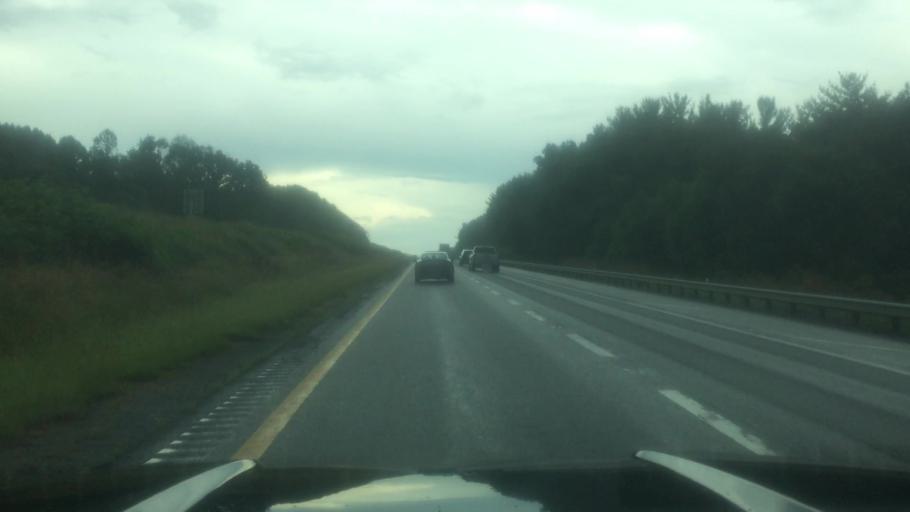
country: US
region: Virginia
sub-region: Carroll County
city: Hillsville
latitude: 36.6822
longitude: -80.7169
